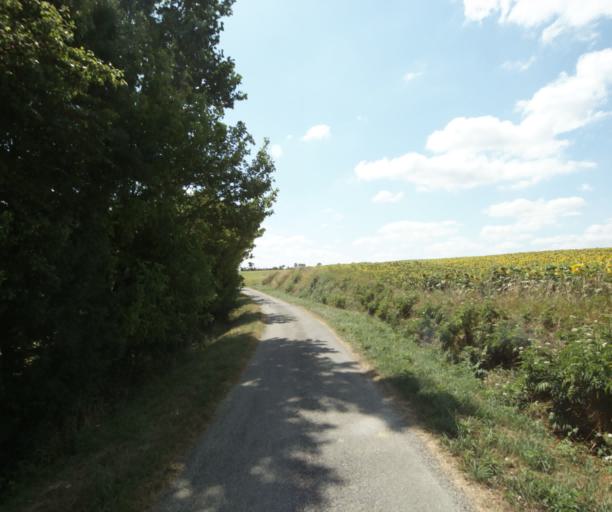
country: FR
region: Midi-Pyrenees
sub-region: Departement de la Haute-Garonne
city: Saint-Felix-Lauragais
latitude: 43.4686
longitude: 1.8391
